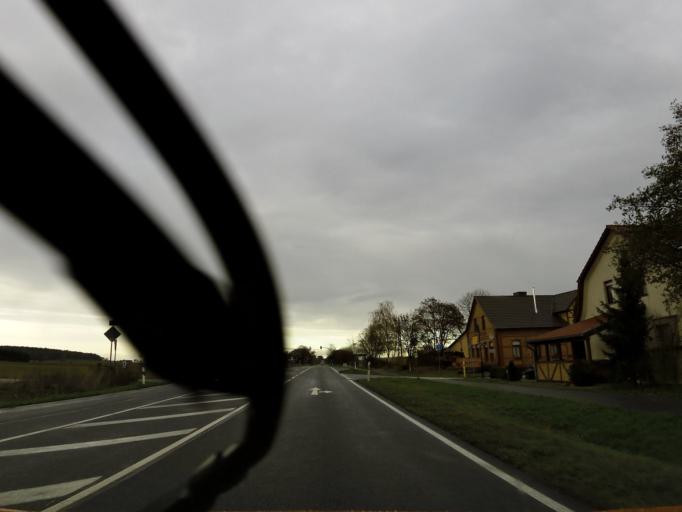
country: DE
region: Saxony-Anhalt
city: Gardelegen
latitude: 52.5615
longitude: 11.3615
